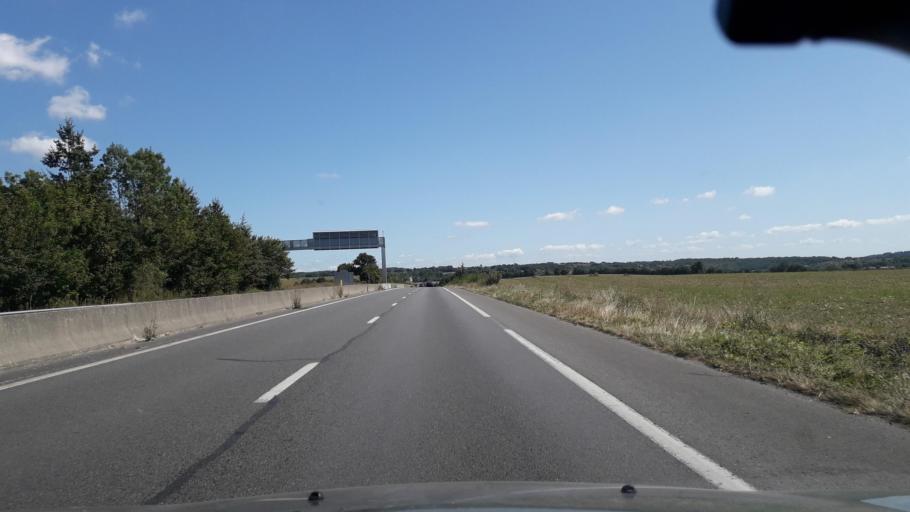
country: FR
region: Poitou-Charentes
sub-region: Departement de la Charente
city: Ruelle-sur-Touvre
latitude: 45.6868
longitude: 0.2126
